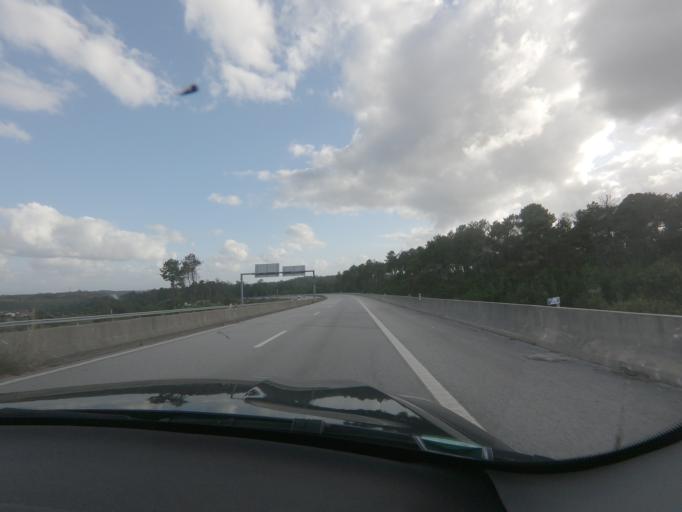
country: PT
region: Viseu
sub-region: Viseu
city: Abraveses
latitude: 40.6673
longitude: -7.9701
